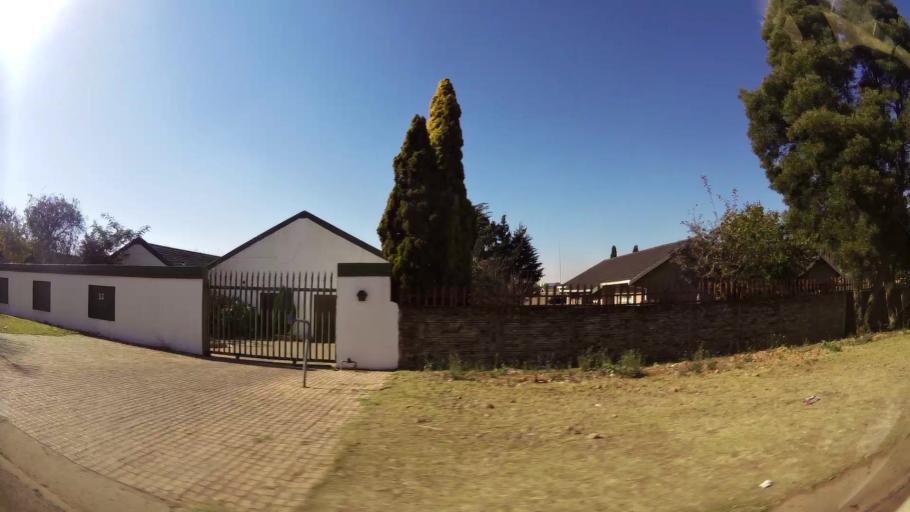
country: ZA
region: Mpumalanga
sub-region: Nkangala District Municipality
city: Witbank
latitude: -25.8756
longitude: 29.2494
